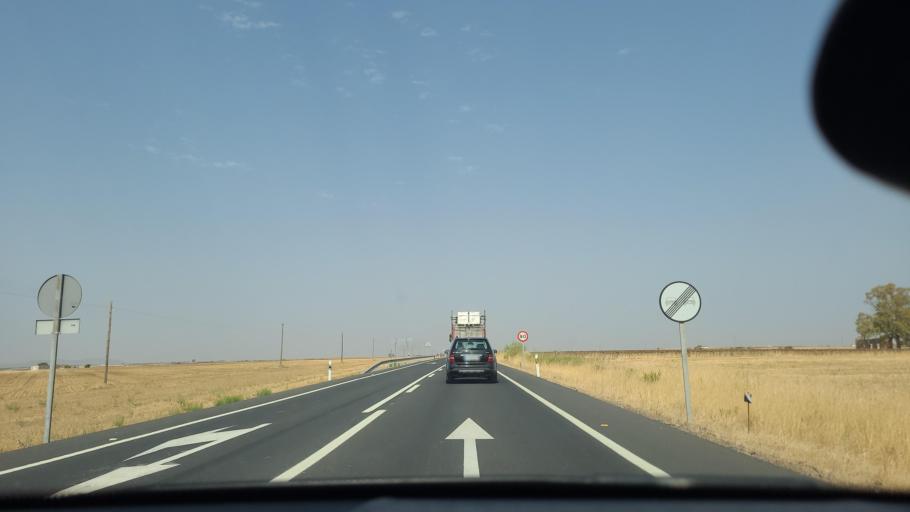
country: ES
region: Extremadura
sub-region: Provincia de Badajoz
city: Azuaga
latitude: 38.2598
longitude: -5.7202
